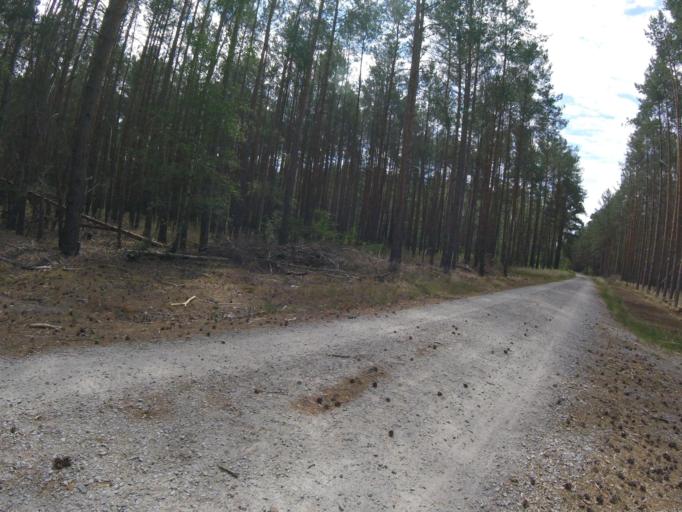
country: DE
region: Brandenburg
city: Gross Koris
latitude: 52.1388
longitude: 13.6608
